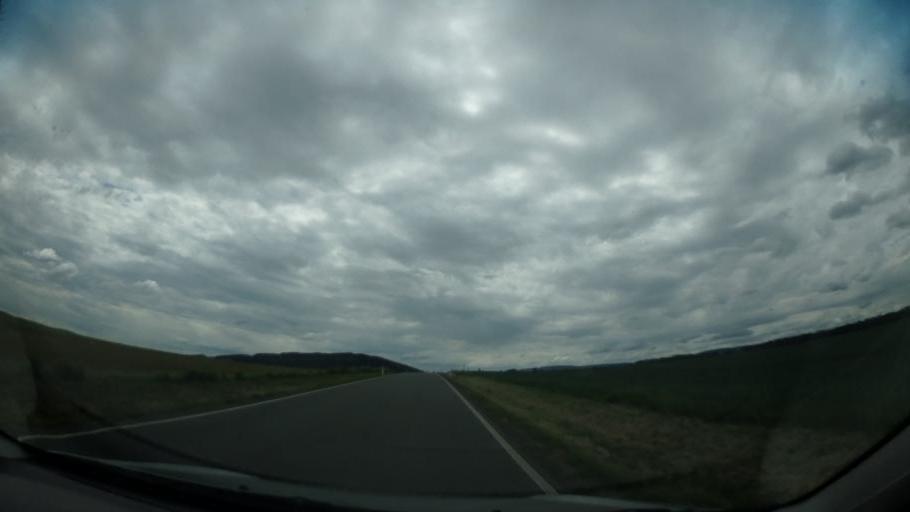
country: CZ
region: Pardubicky
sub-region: Okres Svitavy
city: Moravska Trebova
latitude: 49.8095
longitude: 16.6890
